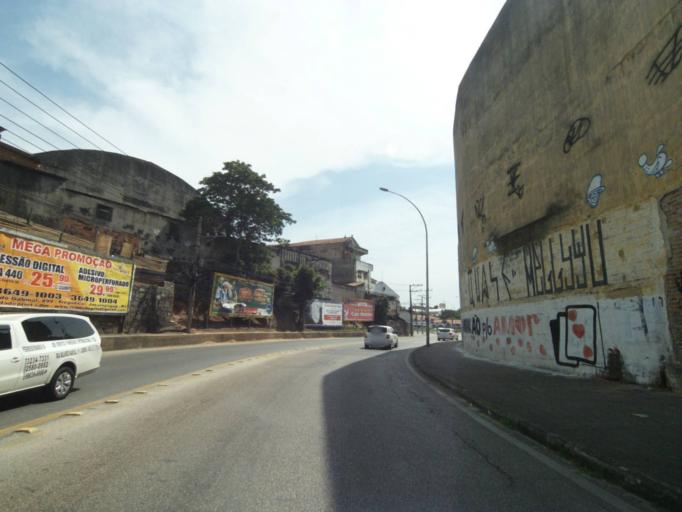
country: BR
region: Rio de Janeiro
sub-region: Rio De Janeiro
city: Rio de Janeiro
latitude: -22.8699
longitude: -43.2488
